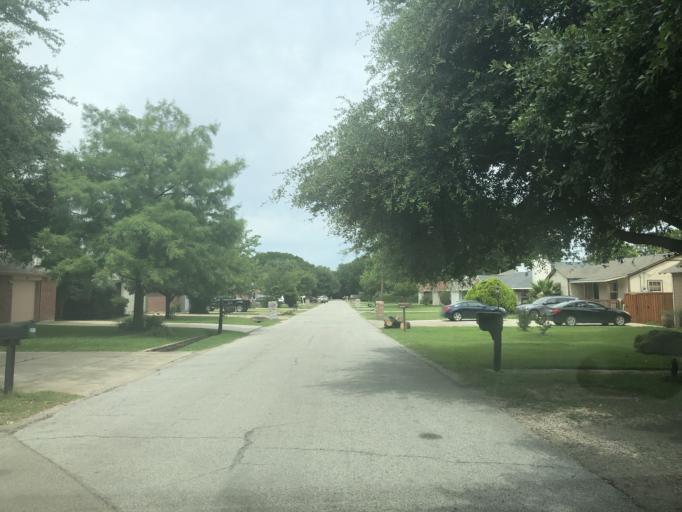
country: US
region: Texas
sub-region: Dallas County
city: Irving
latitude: 32.7943
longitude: -96.9811
